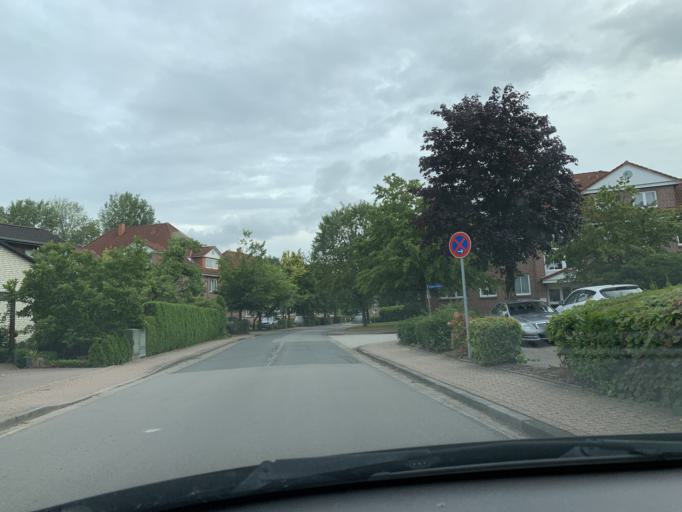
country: DE
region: Lower Saxony
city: Westerstede
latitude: 53.2593
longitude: 7.9357
